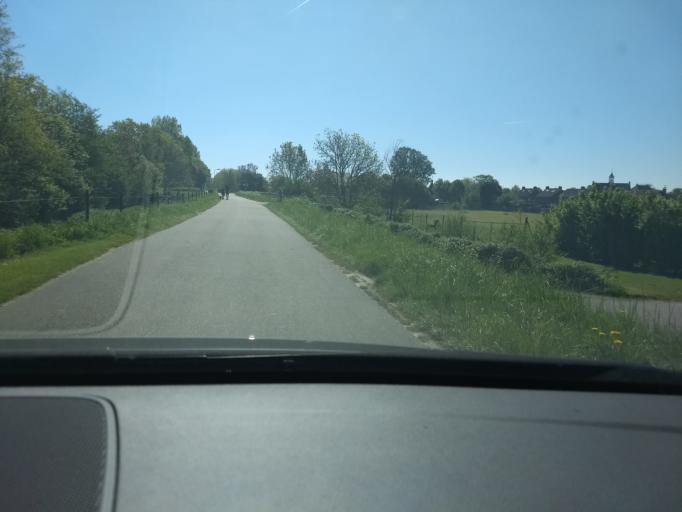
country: NL
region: Zeeland
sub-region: Gemeente Veere
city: Veere
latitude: 51.5798
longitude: 3.6153
